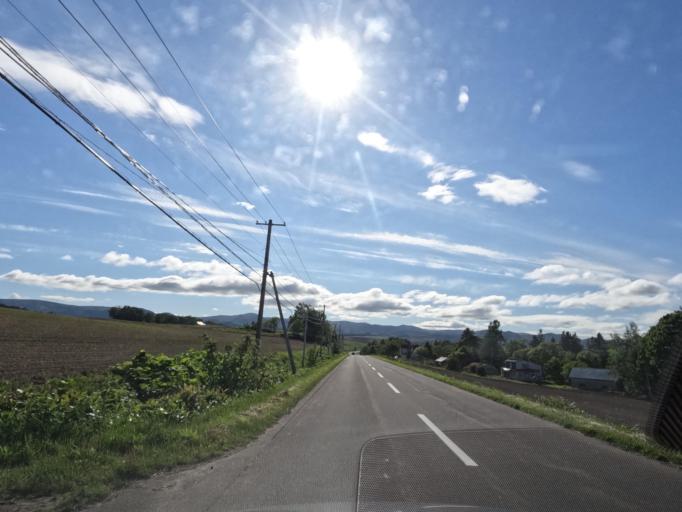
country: JP
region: Hokkaido
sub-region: Asahikawa-shi
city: Asahikawa
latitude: 43.5961
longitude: 142.4446
